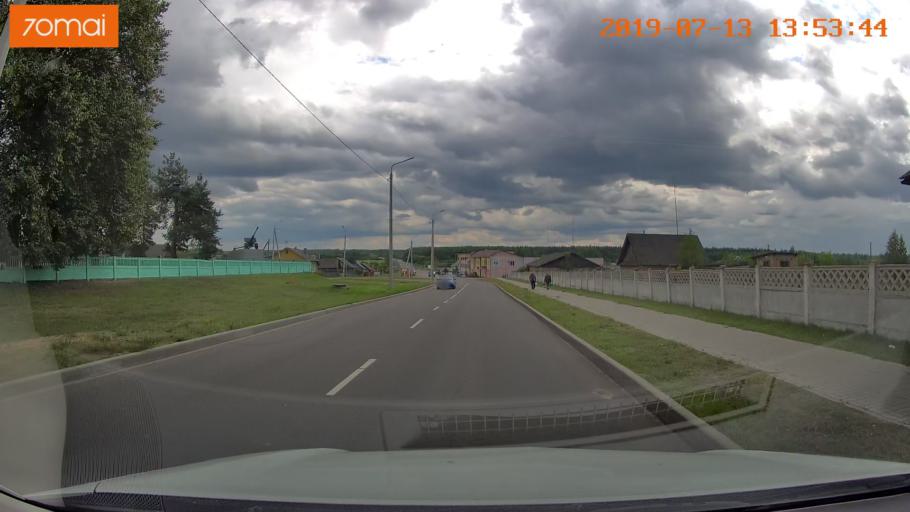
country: BY
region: Mogilev
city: Asipovichy
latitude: 53.2906
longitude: 28.6512
